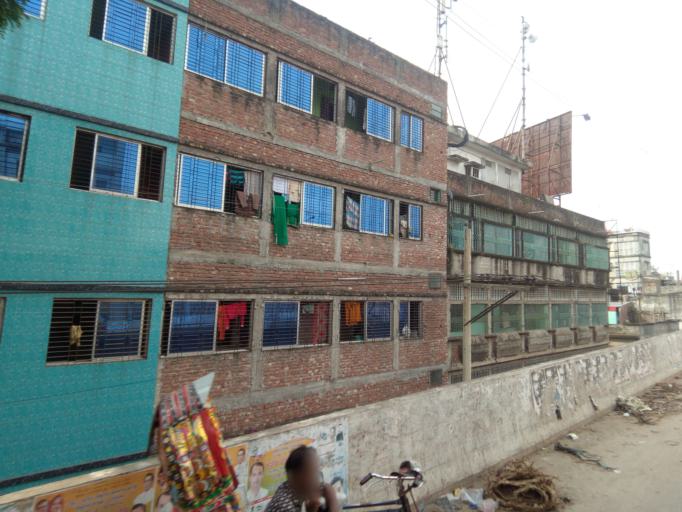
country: BD
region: Dhaka
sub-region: Dhaka
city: Dhaka
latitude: 23.7055
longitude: 90.3995
